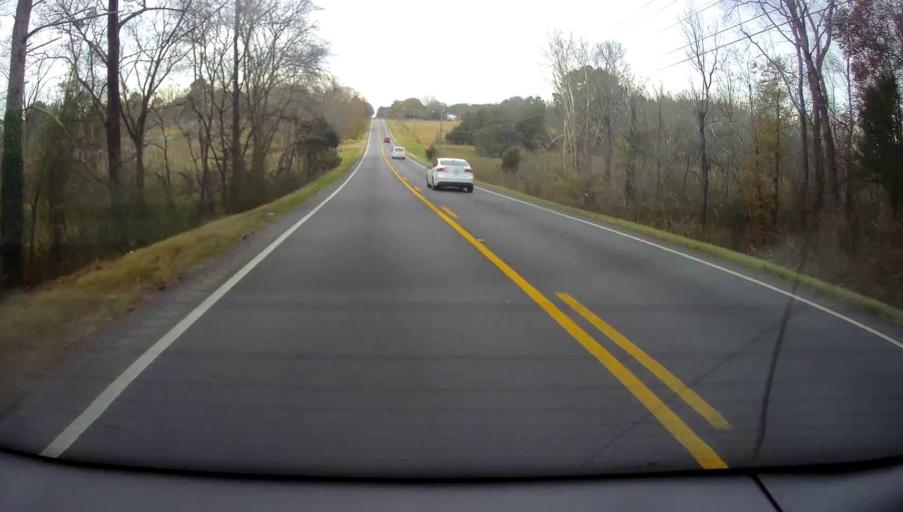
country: US
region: Alabama
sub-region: Morgan County
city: Priceville
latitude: 34.4526
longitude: -86.7665
